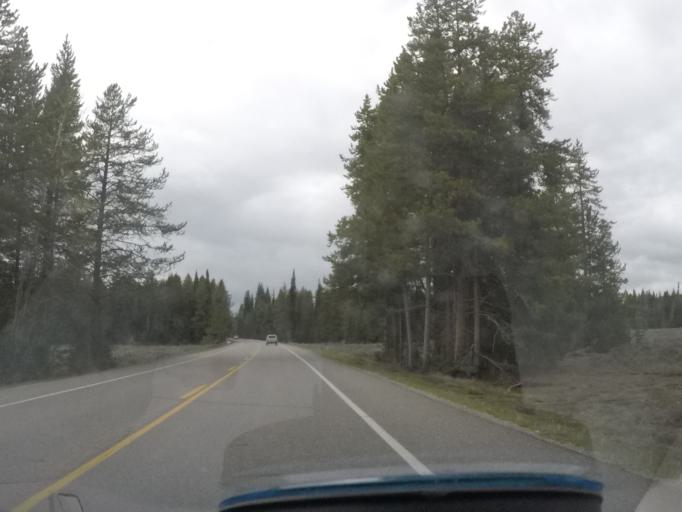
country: US
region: Wyoming
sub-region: Teton County
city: Jackson
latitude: 43.9011
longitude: -110.5802
